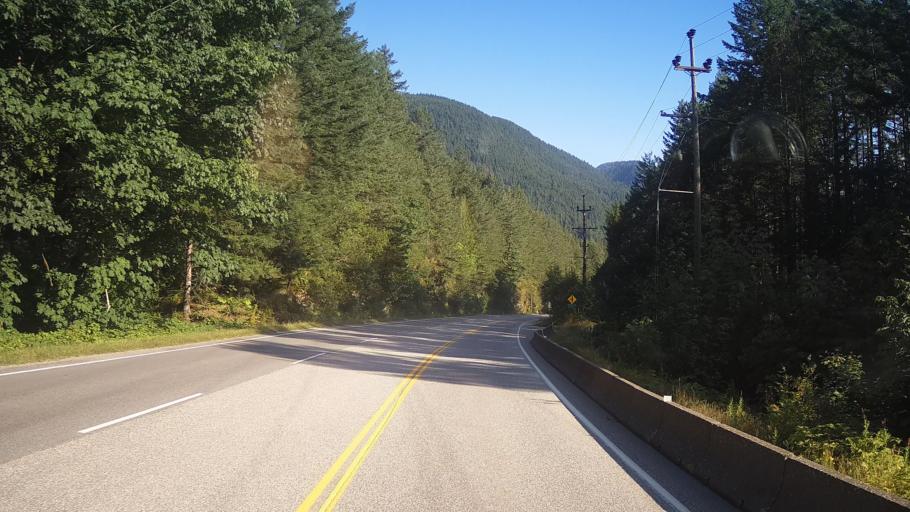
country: CA
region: British Columbia
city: Hope
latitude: 49.4219
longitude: -121.4377
